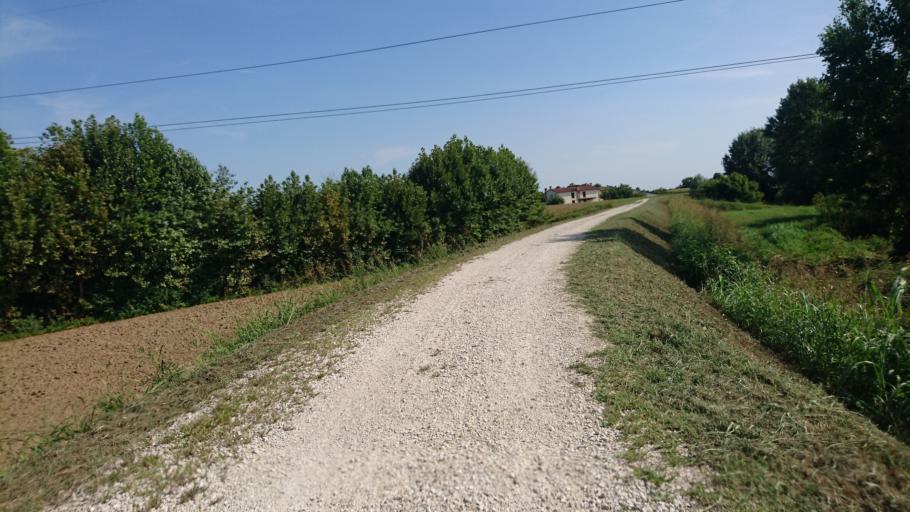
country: IT
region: Veneto
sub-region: Provincia di Padova
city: Veggiano
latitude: 45.4447
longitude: 11.7260
